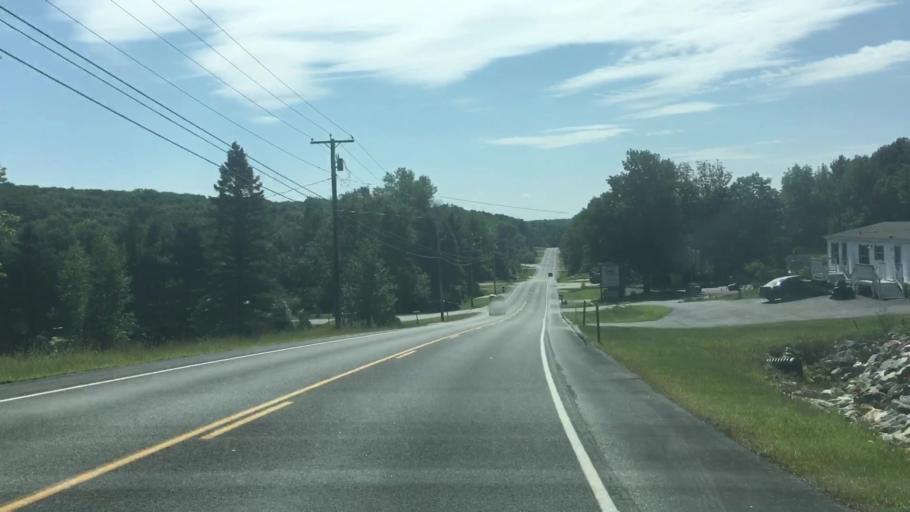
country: US
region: Maine
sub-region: Androscoggin County
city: Sabattus
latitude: 44.0839
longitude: -70.0794
